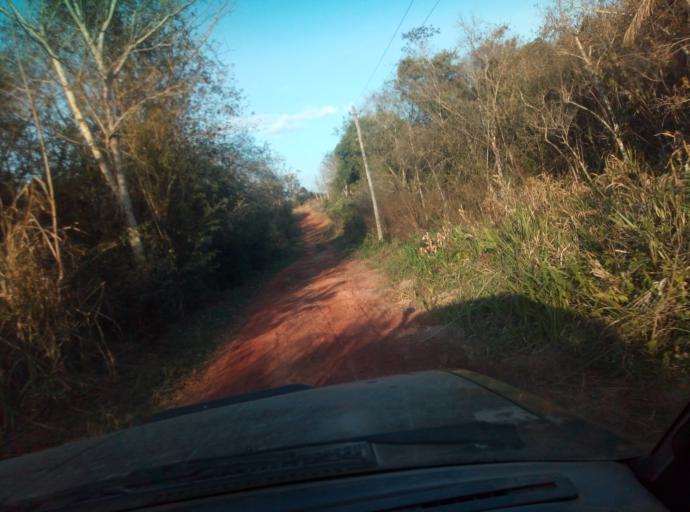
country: PY
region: Caaguazu
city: Doctor Cecilio Baez
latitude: -25.1532
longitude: -56.2380
